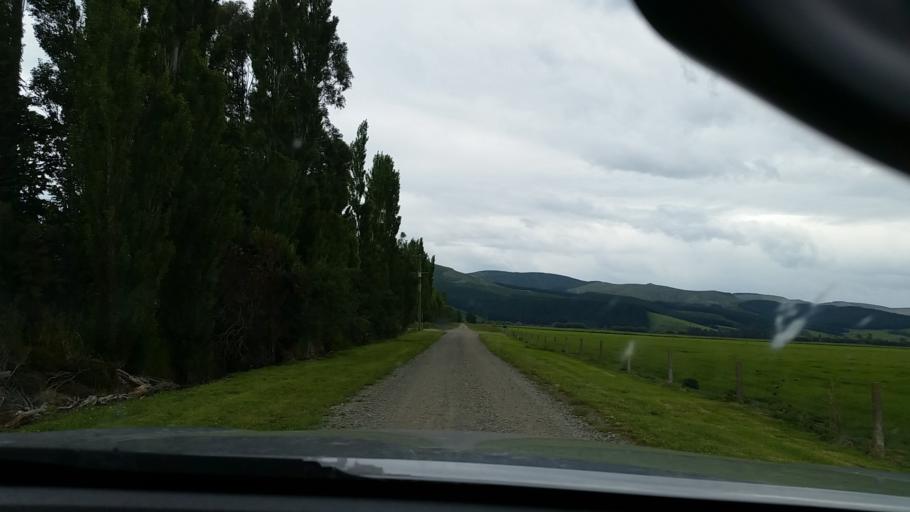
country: NZ
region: Southland
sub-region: Southland District
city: Winton
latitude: -45.9513
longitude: 168.3205
